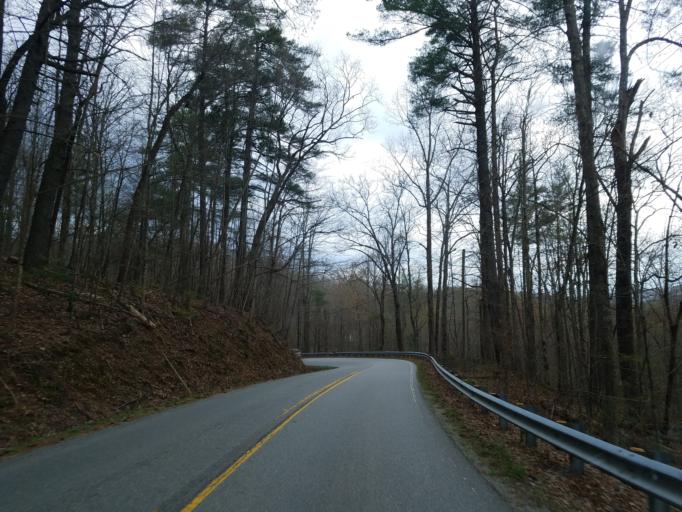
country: US
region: Georgia
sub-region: Lumpkin County
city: Dahlonega
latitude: 34.7033
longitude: -84.0483
